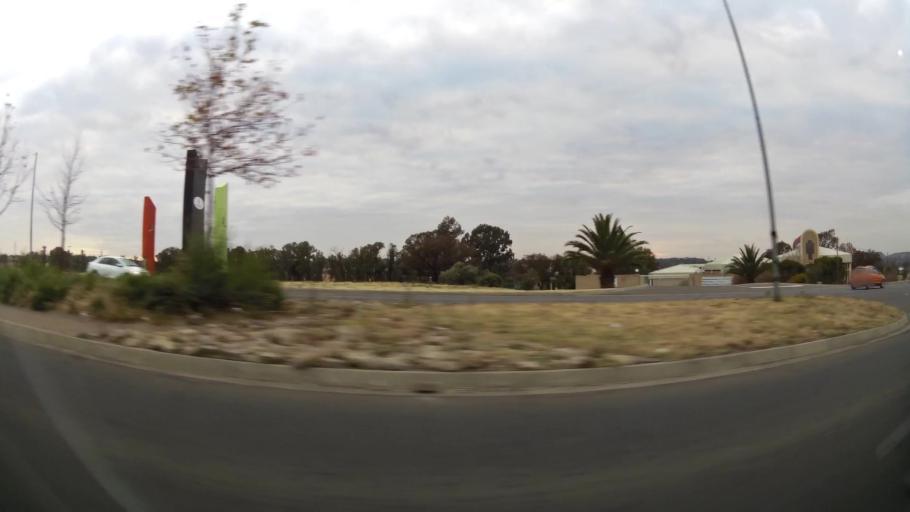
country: ZA
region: Orange Free State
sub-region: Mangaung Metropolitan Municipality
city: Bloemfontein
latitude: -29.0933
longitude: 26.1743
